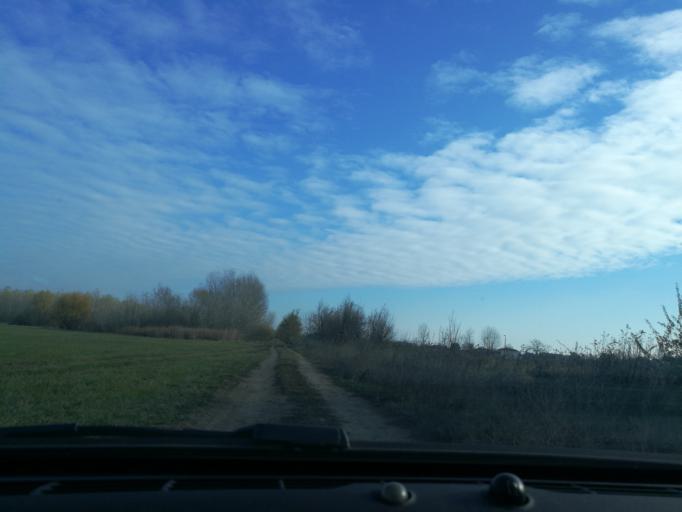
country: HU
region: Szabolcs-Szatmar-Bereg
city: Nyirpazony
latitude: 47.9609
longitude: 21.7755
